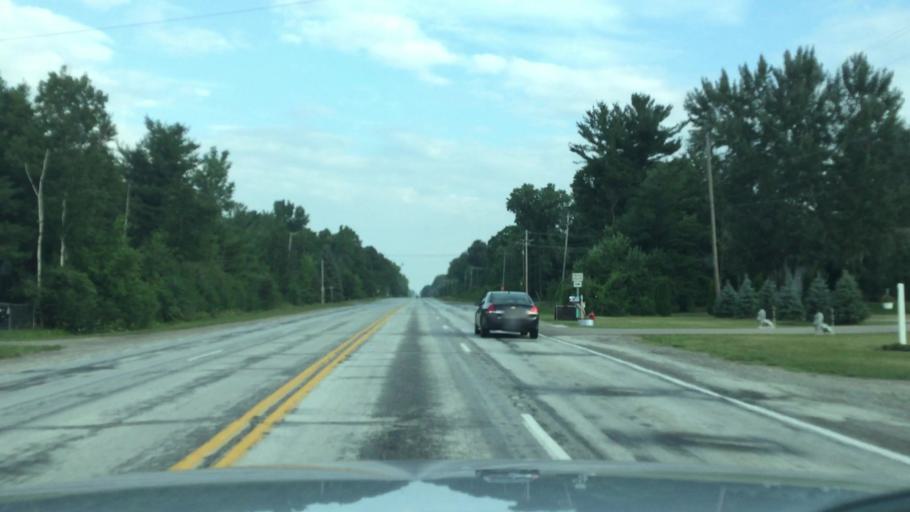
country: US
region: Michigan
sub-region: Saginaw County
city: Birch Run
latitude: 43.2947
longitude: -83.8030
